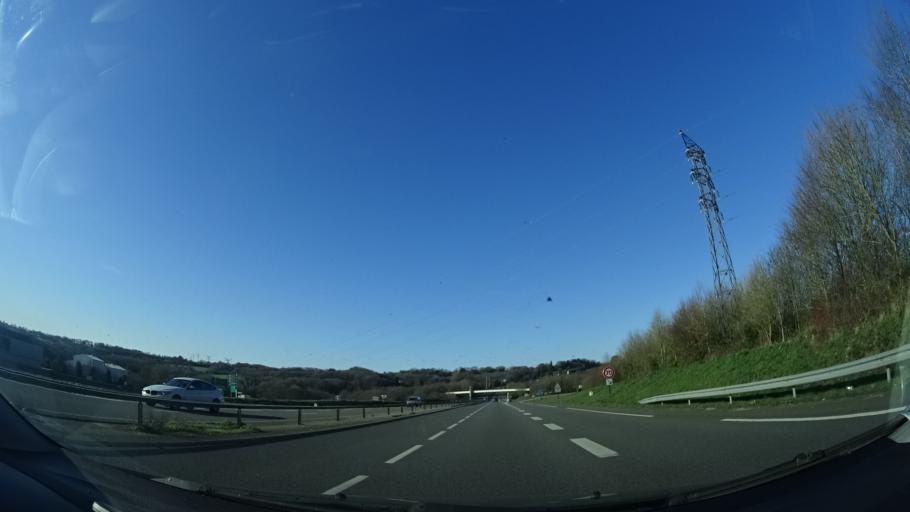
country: FR
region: Brittany
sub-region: Departement du Finistere
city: Morlaix
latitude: 48.5819
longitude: -3.8674
